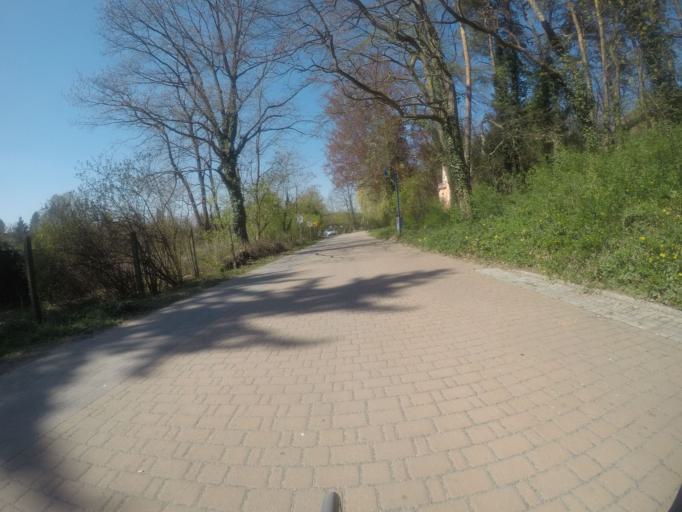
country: DE
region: Brandenburg
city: Rudnitz
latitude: 52.7300
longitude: 13.5886
